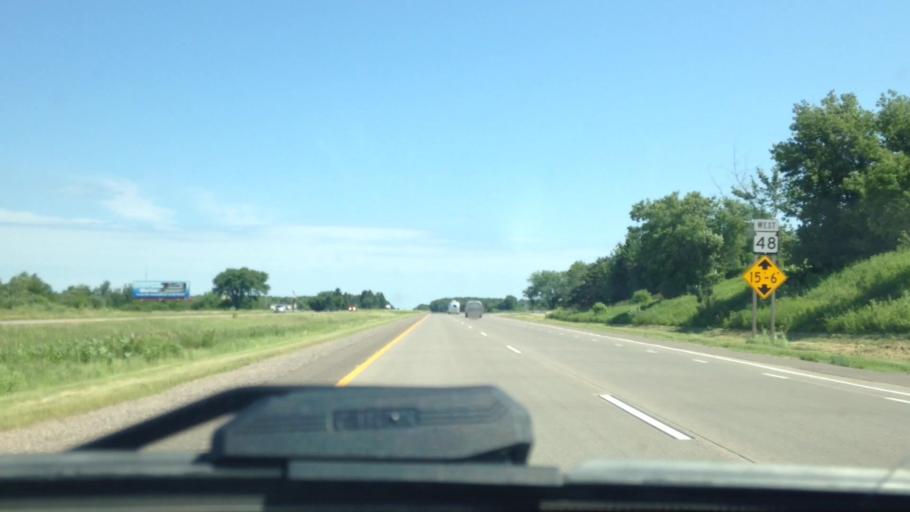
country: US
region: Wisconsin
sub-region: Barron County
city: Rice Lake
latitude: 45.5026
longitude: -91.7635
